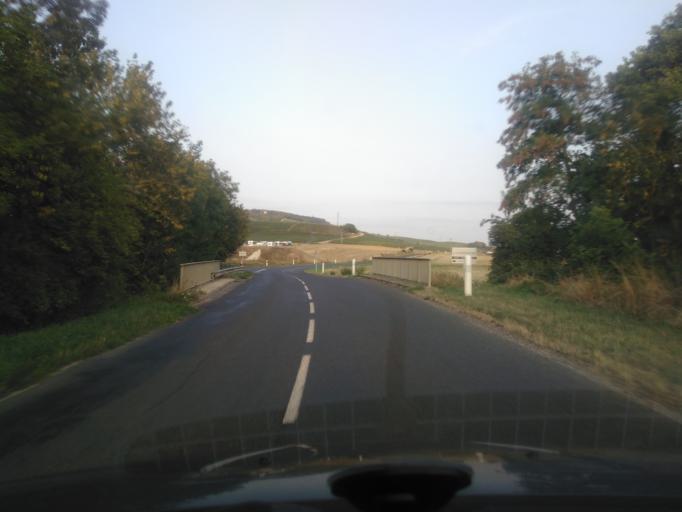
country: FR
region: Champagne-Ardenne
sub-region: Departement de la Marne
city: Mareuil-le-Port
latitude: 49.0882
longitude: 3.7784
